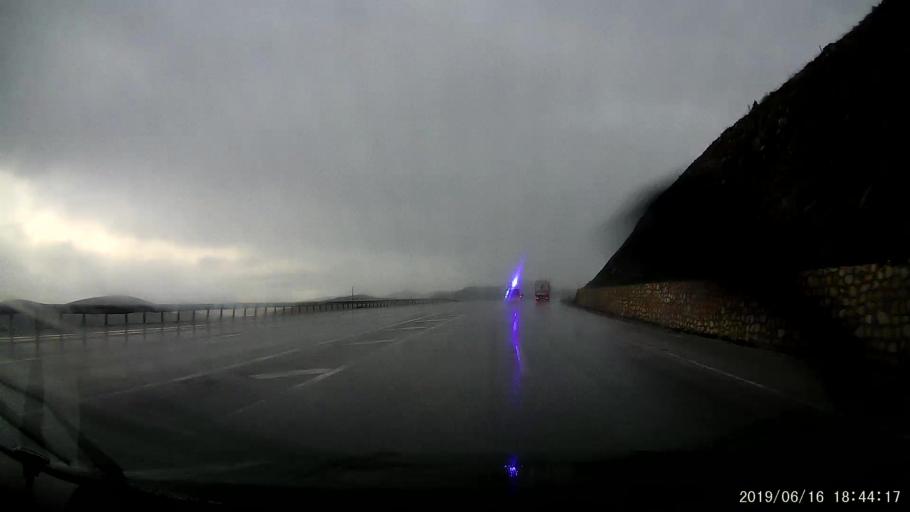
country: TR
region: Erzincan
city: Doganbeyli
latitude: 39.8695
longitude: 39.0759
